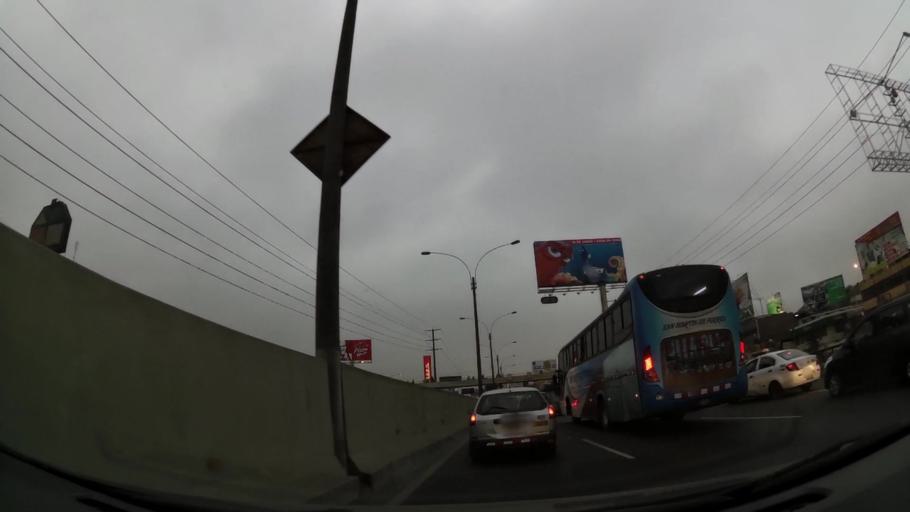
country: PE
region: Lima
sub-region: Lima
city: Independencia
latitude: -11.9939
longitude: -77.0635
